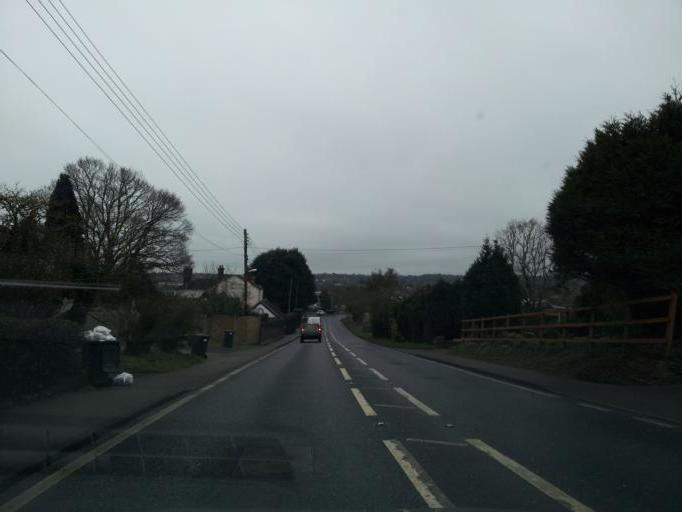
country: GB
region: England
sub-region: Essex
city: Manningtree
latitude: 51.9617
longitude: 1.0621
